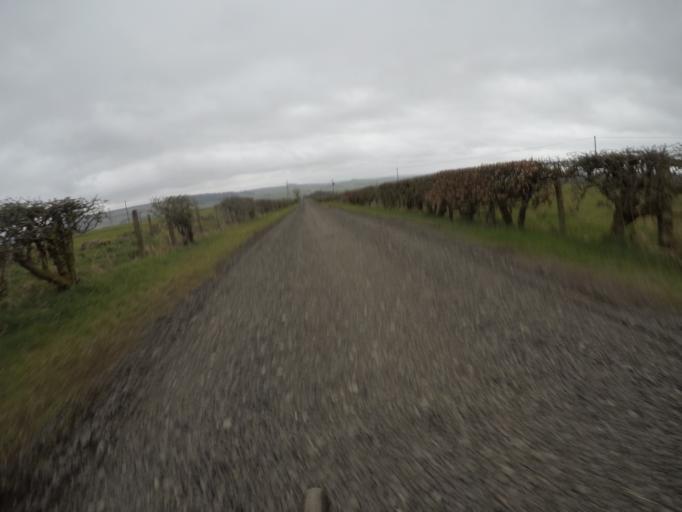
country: GB
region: Scotland
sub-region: East Ayrshire
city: Newmilns
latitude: 55.6224
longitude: -4.3428
